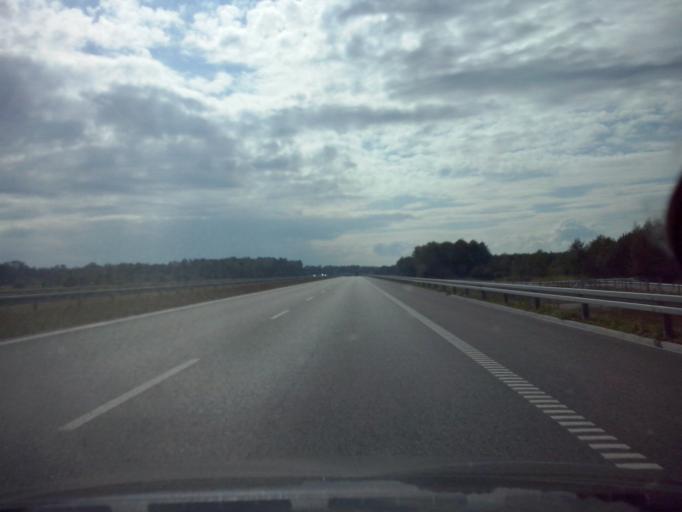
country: PL
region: Lesser Poland Voivodeship
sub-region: Powiat tarnowski
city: Lisia Gora
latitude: 50.0721
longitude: 21.0828
